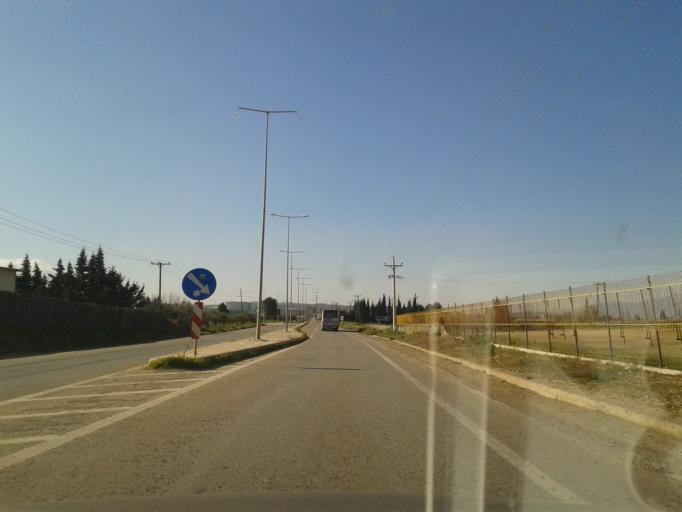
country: GR
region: Central Greece
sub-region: Nomos Voiotias
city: Thivai
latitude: 38.3384
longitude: 23.3498
